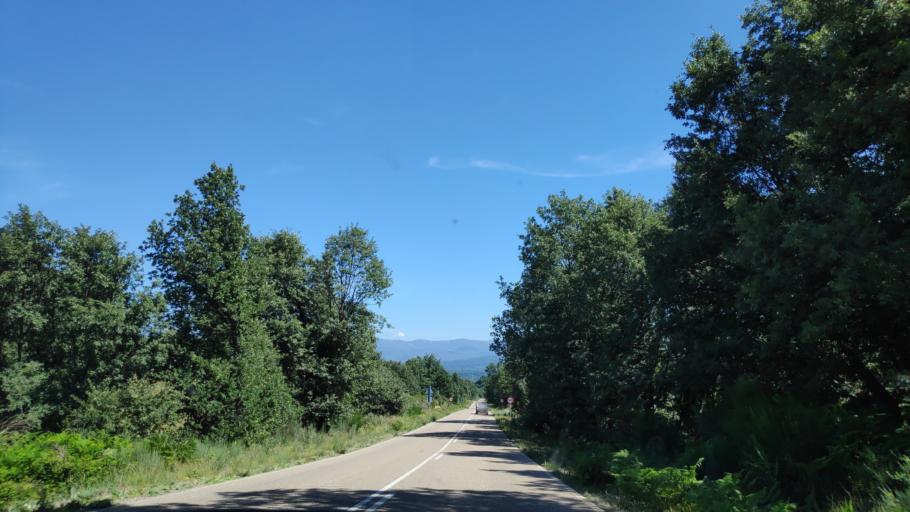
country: ES
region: Castille and Leon
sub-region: Provincia de Zamora
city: Cobreros
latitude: 42.0272
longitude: -6.6808
